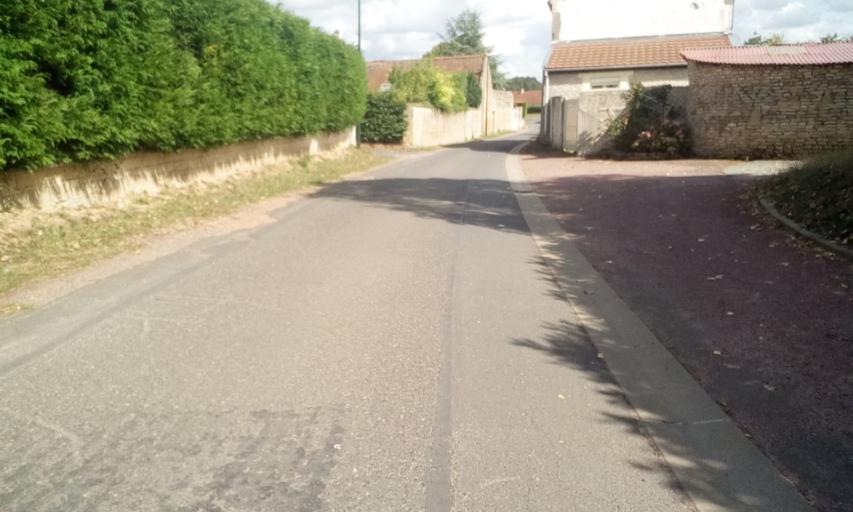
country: FR
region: Lower Normandy
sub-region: Departement du Calvados
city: Saint-Sylvain
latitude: 49.0882
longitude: -0.2011
